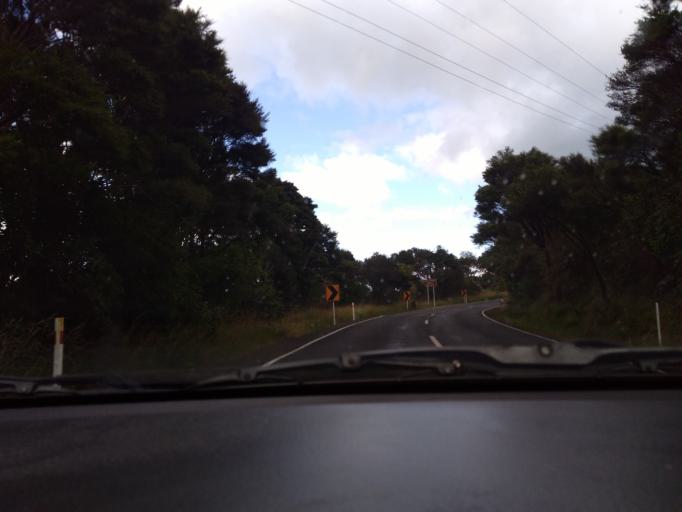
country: NZ
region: Auckland
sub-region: Auckland
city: Titirangi
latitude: -37.0065
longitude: 174.5818
